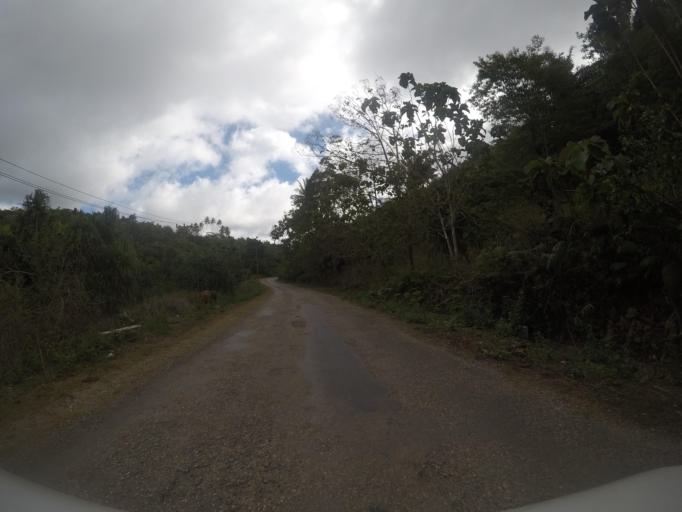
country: TL
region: Lautem
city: Lospalos
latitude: -8.5412
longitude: 126.9530
